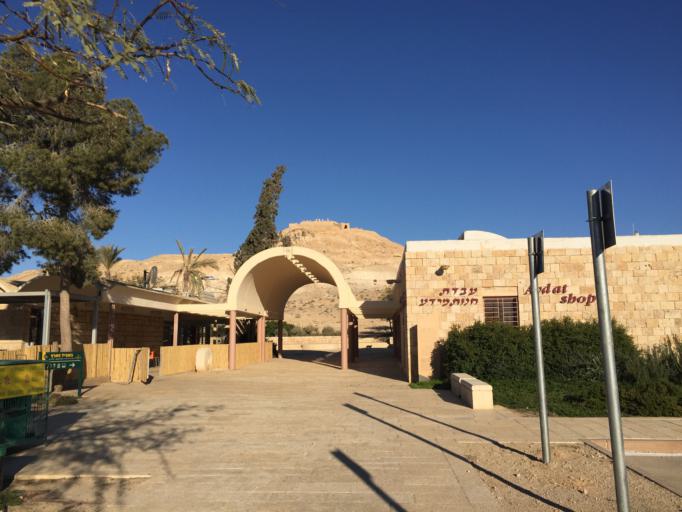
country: IL
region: Southern District
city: Midreshet Ben-Gurion
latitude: 30.7922
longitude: 34.7689
